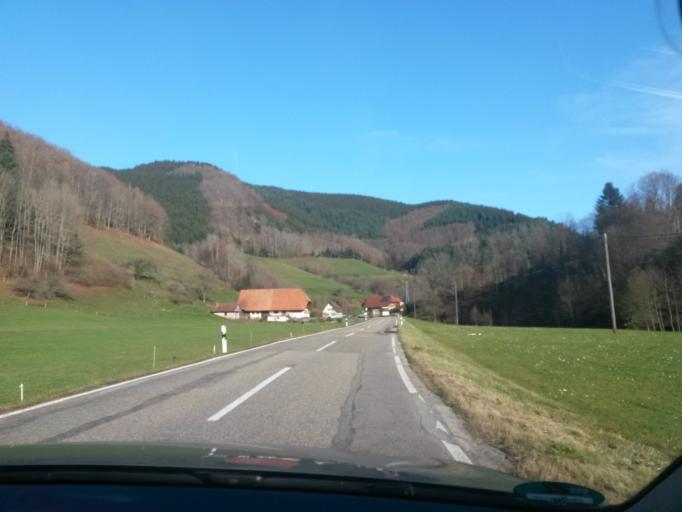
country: DE
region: Baden-Wuerttemberg
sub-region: Freiburg Region
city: Oberwolfach
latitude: 48.3512
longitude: 8.2396
